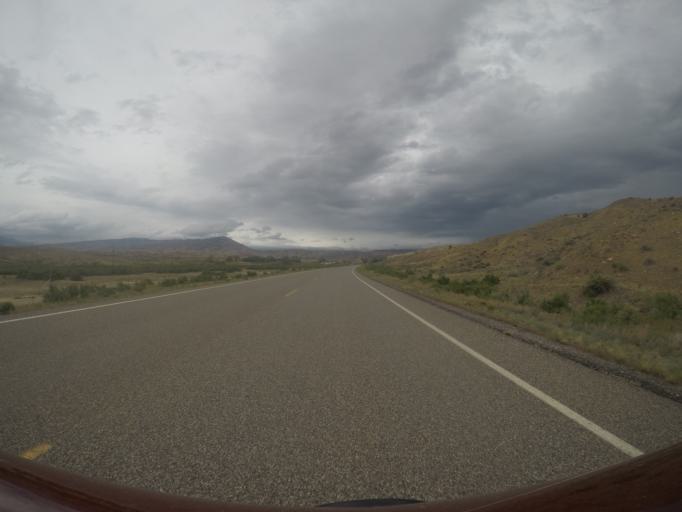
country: US
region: Wyoming
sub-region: Big Horn County
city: Lovell
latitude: 44.9537
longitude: -108.2944
